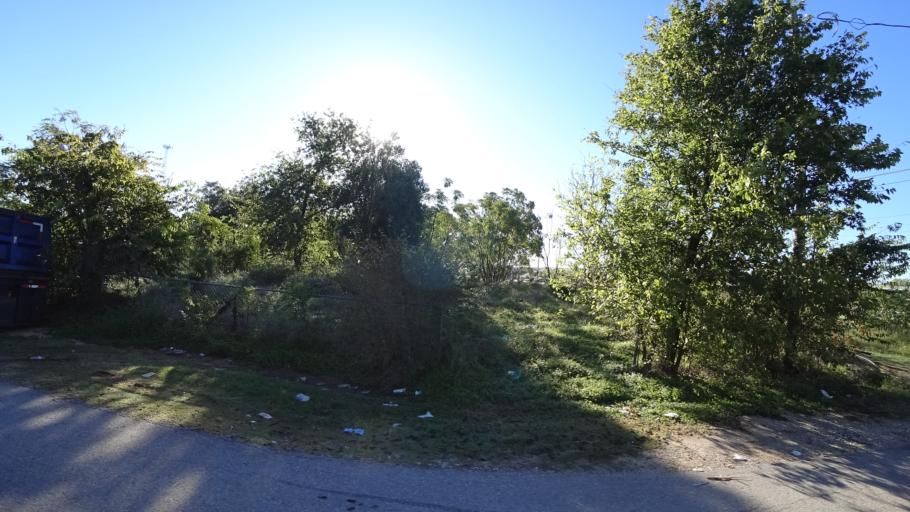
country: US
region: Texas
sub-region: Travis County
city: Hornsby Bend
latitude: 30.2046
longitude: -97.6411
